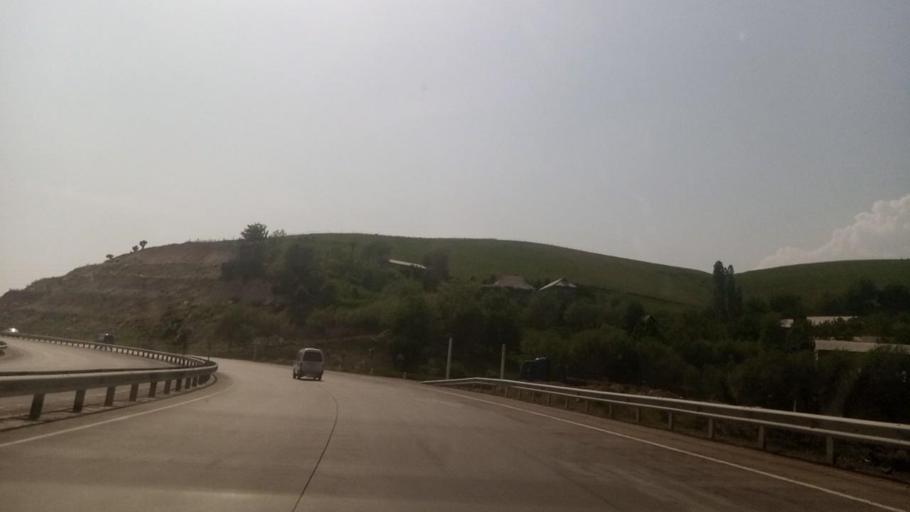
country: UZ
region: Toshkent
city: Angren
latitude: 41.0678
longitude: 70.2215
